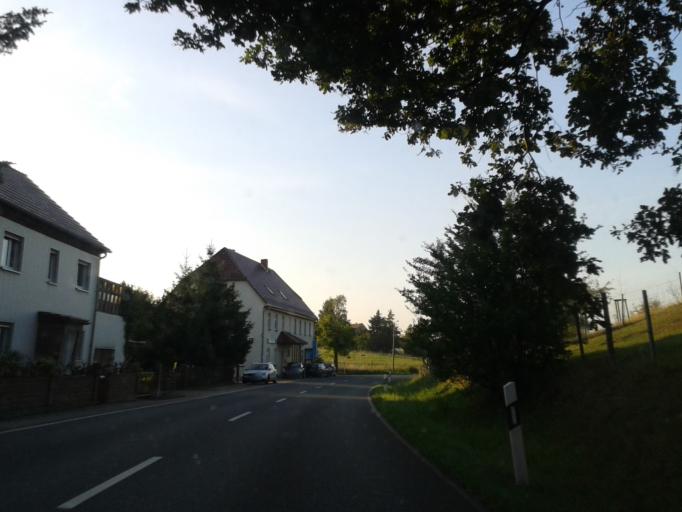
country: DE
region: Saxony
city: Klipphausen
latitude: 51.1018
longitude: 13.4892
